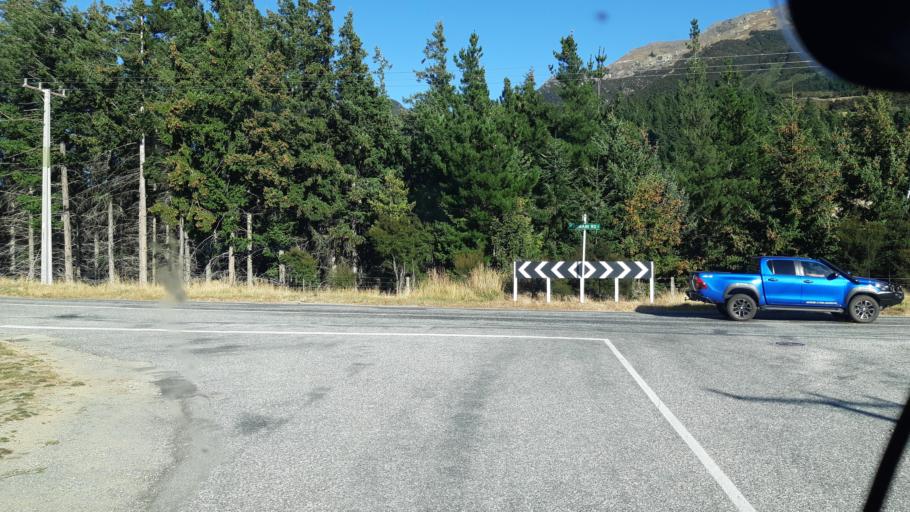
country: NZ
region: Otago
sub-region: Queenstown-Lakes District
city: Wanaka
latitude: -44.6128
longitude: 169.2526
